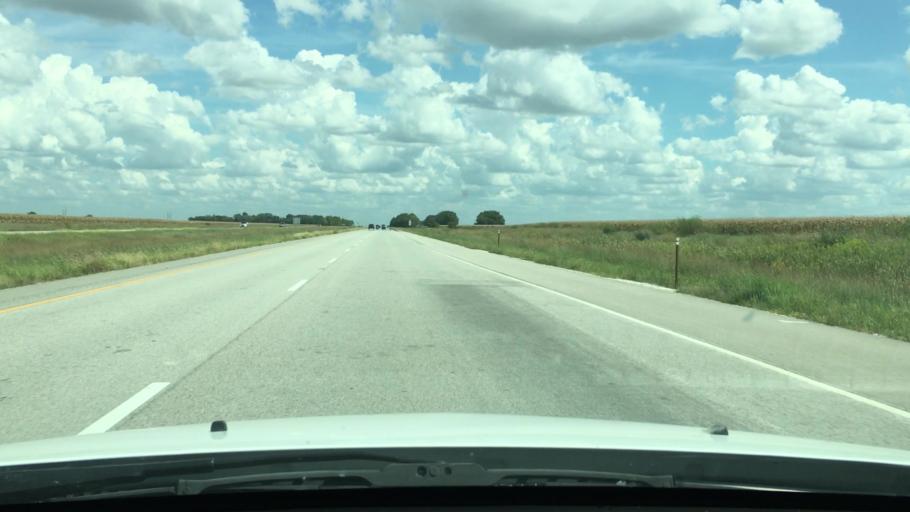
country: US
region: Illinois
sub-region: Sangamon County
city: New Berlin
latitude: 39.7368
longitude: -90.0344
